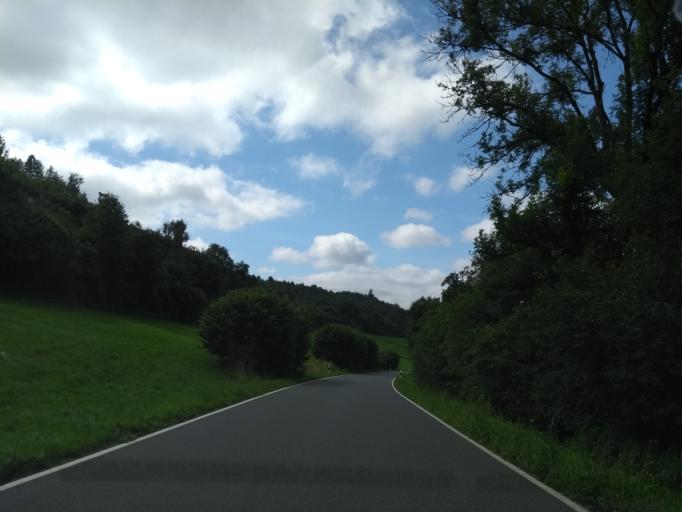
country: DE
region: North Rhine-Westphalia
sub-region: Regierungsbezirk Detmold
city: Lugde
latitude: 51.9509
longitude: 9.2673
